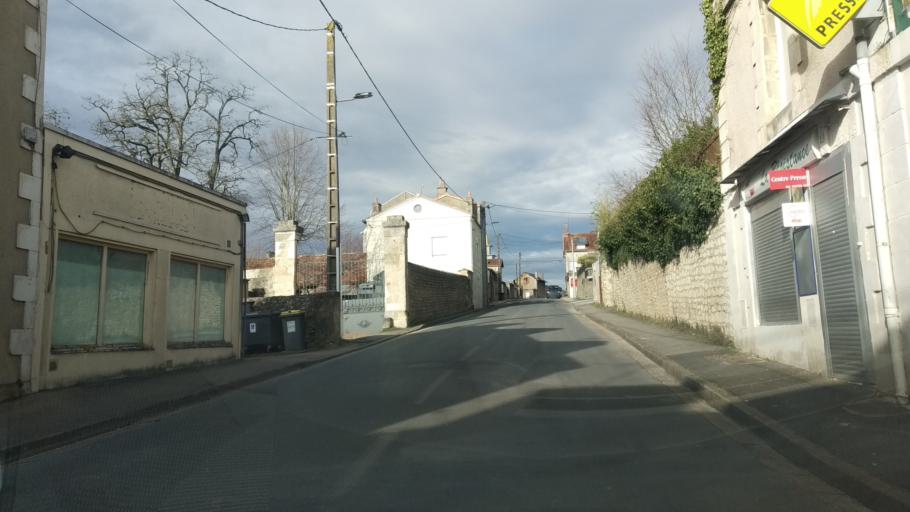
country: FR
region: Poitou-Charentes
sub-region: Departement de la Vienne
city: Poitiers
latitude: 46.5933
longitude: 0.3403
